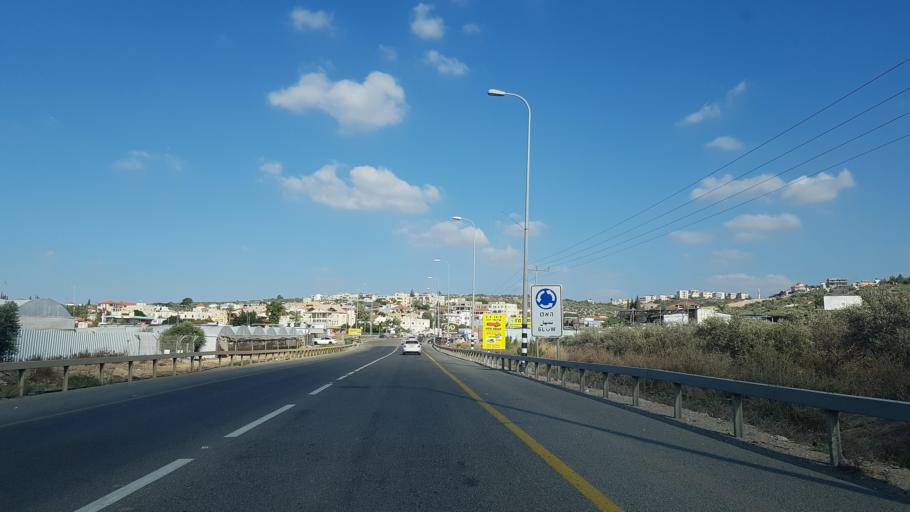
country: PS
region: West Bank
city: Zayta
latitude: 32.3597
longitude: 35.0266
